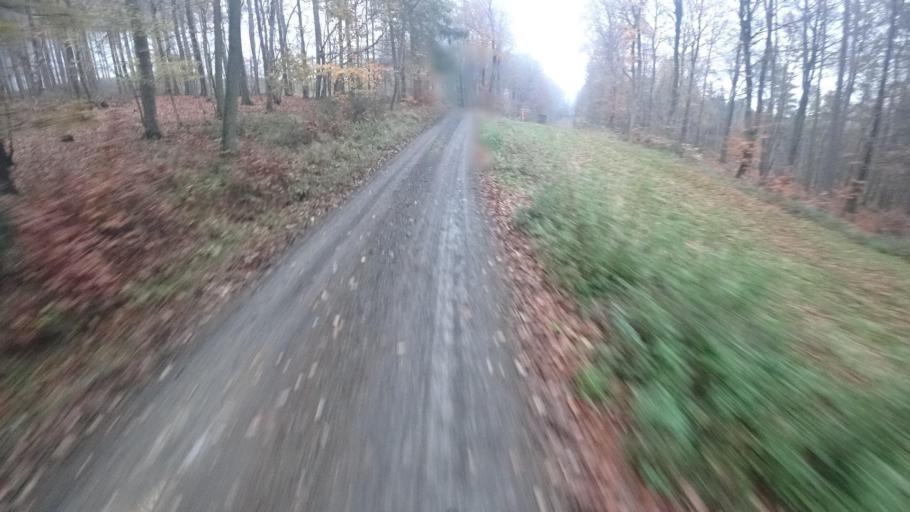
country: DE
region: Rheinland-Pfalz
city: Dernau
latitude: 50.5041
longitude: 7.0682
